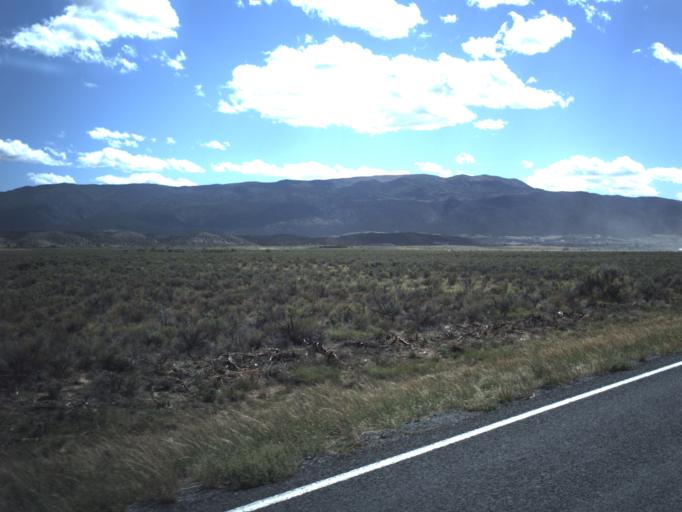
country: US
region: Utah
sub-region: Iron County
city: Enoch
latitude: 37.8234
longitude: -113.0504
